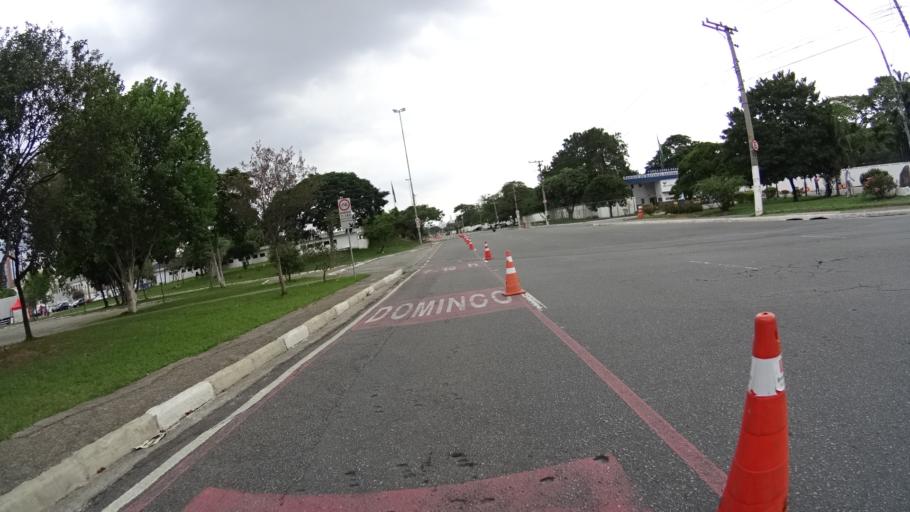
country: BR
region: Sao Paulo
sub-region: Sao Paulo
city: Sao Paulo
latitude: -23.5046
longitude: -46.6284
